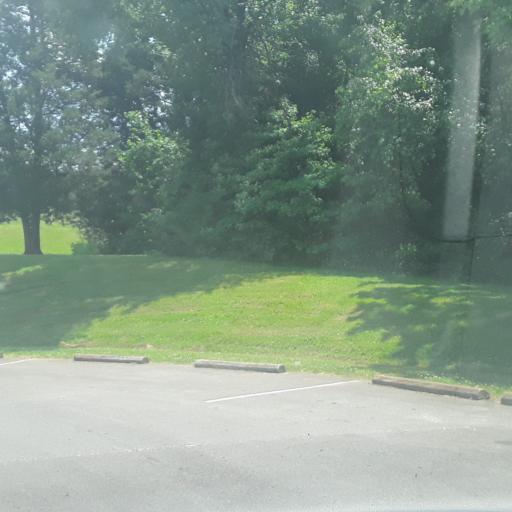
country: US
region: Tennessee
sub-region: Williamson County
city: Brentwood Estates
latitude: 36.0560
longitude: -86.7073
